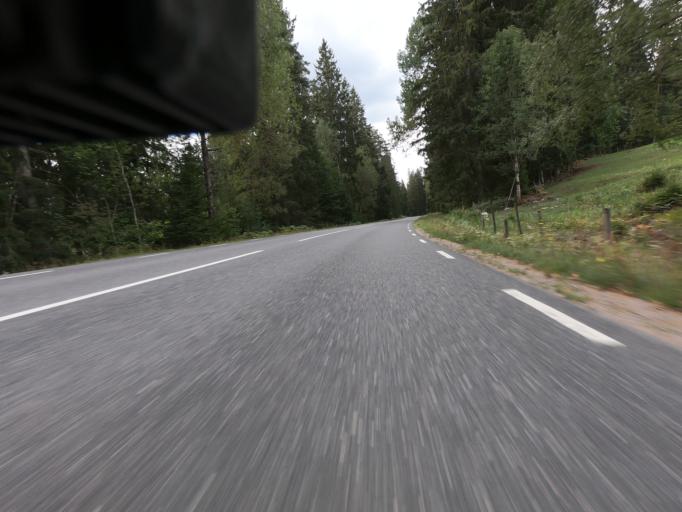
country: SE
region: Joenkoeping
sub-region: Vetlanda Kommun
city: Landsbro
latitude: 57.2412
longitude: 14.9503
